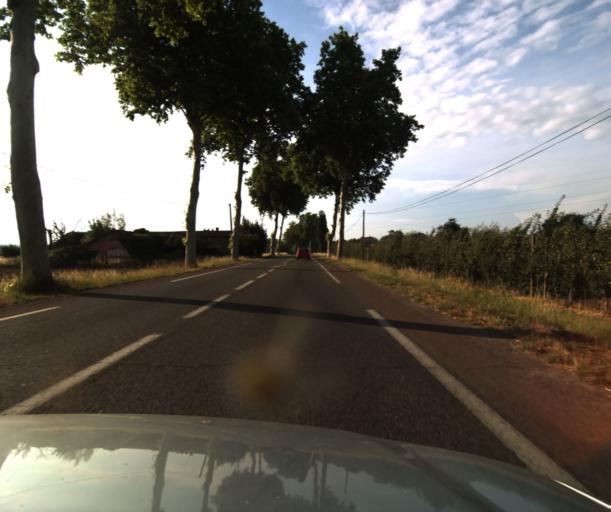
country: FR
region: Midi-Pyrenees
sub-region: Departement du Tarn-et-Garonne
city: Castelsarrasin
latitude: 44.0670
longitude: 1.0959
